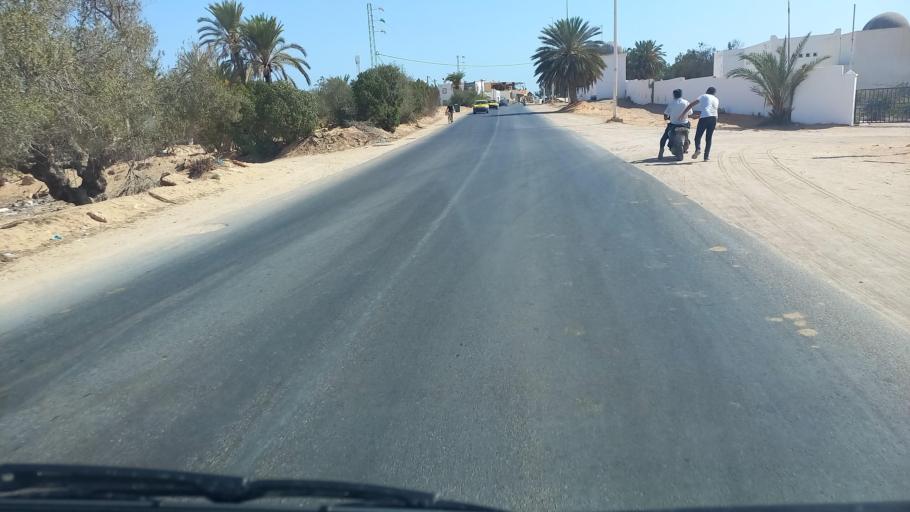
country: TN
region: Madanin
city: Midoun
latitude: 33.7797
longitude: 11.0415
